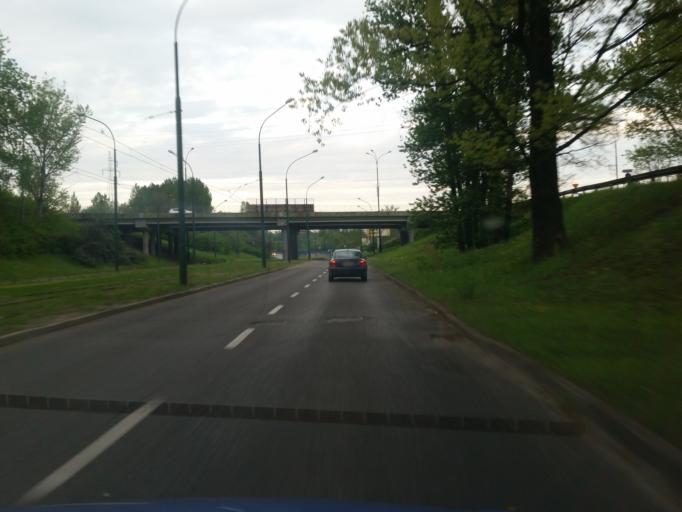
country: PL
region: Silesian Voivodeship
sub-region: Powiat bedzinski
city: Bedzin
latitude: 50.2934
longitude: 19.1665
